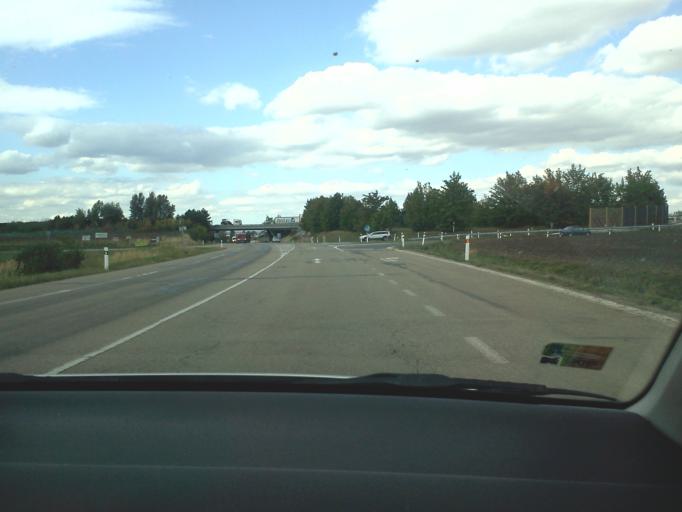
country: CZ
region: Central Bohemia
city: Prerov nad Labem
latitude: 50.1347
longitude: 14.8459
